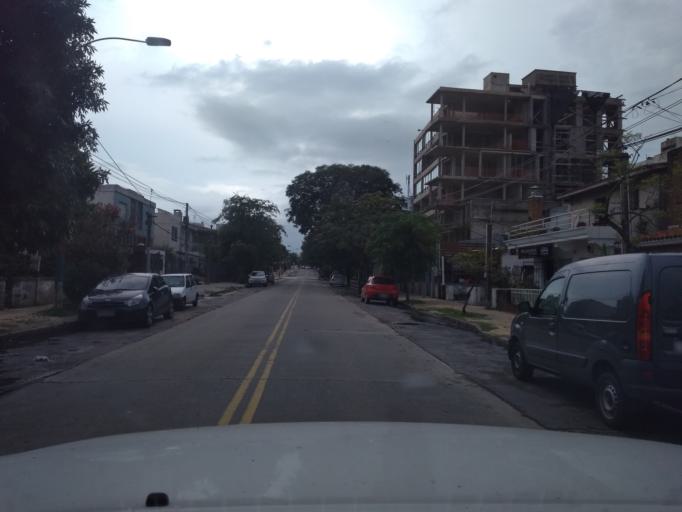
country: UY
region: Canelones
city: Paso de Carrasco
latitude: -34.8959
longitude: -56.0991
